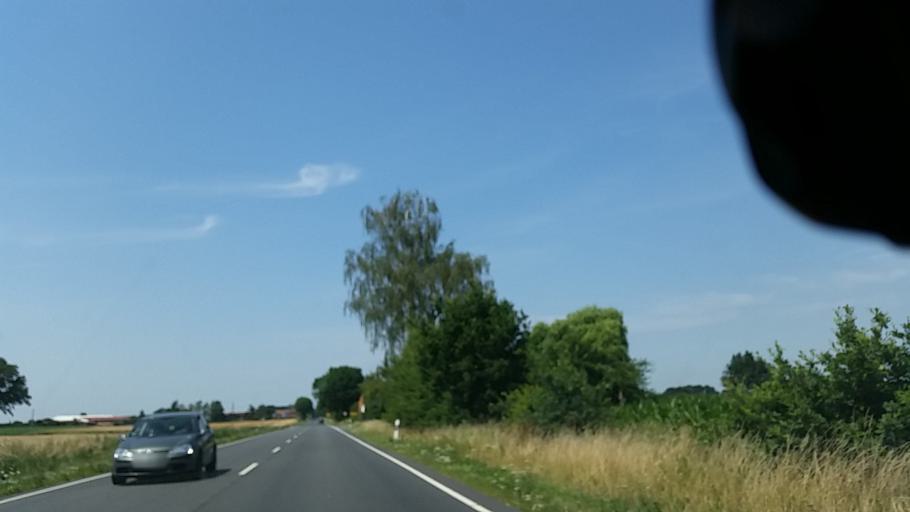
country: DE
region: Lower Saxony
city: Wietzen
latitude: 52.7220
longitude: 9.0530
